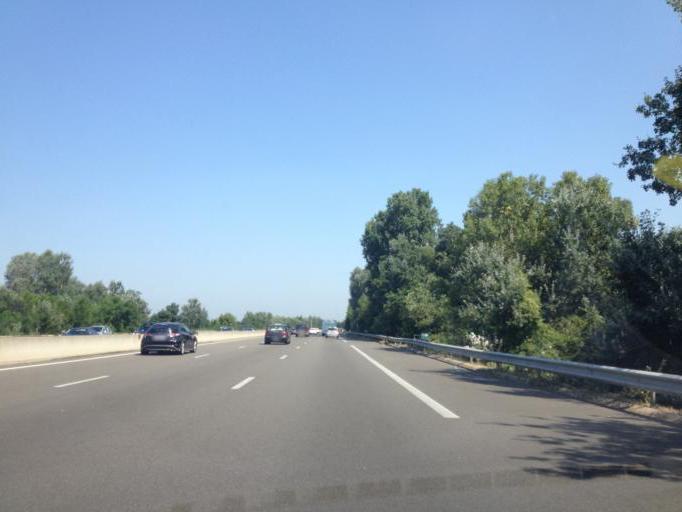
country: FR
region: Provence-Alpes-Cote d'Azur
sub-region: Departement du Vaucluse
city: Mondragon
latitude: 44.2304
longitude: 4.7094
